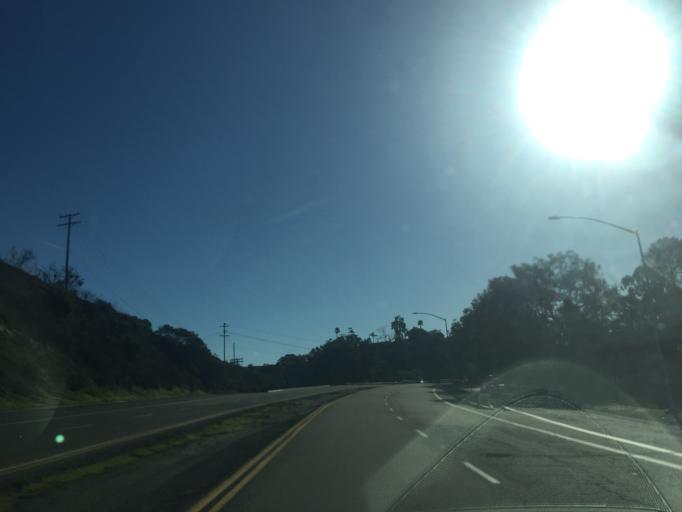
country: US
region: California
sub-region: San Diego County
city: Lemon Grove
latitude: 32.7645
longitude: -117.0970
